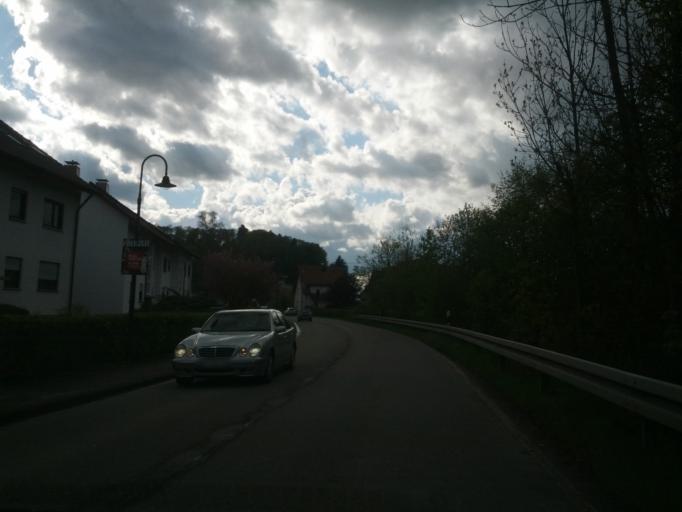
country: DE
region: Baden-Wuerttemberg
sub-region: Freiburg Region
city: Heuweiler
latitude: 48.0525
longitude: 7.9304
